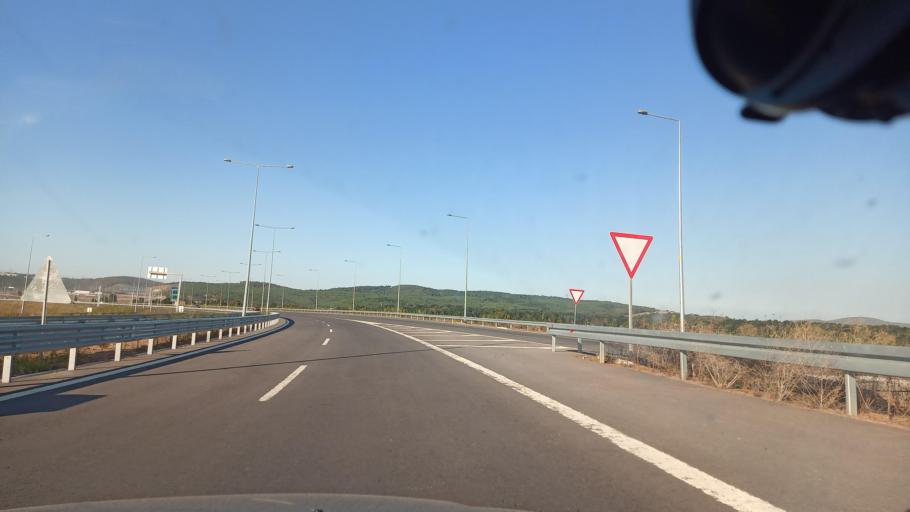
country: TR
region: Sakarya
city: Kazimpasa
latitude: 40.8283
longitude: 30.3517
